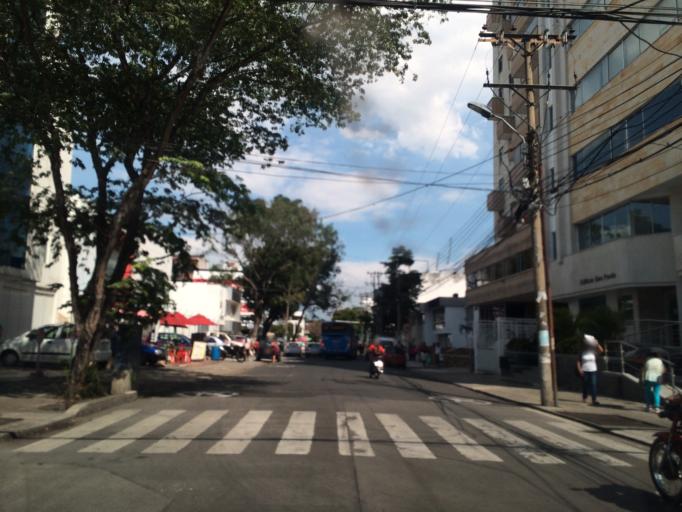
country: CO
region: Valle del Cauca
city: Cali
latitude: 3.4638
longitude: -76.5266
